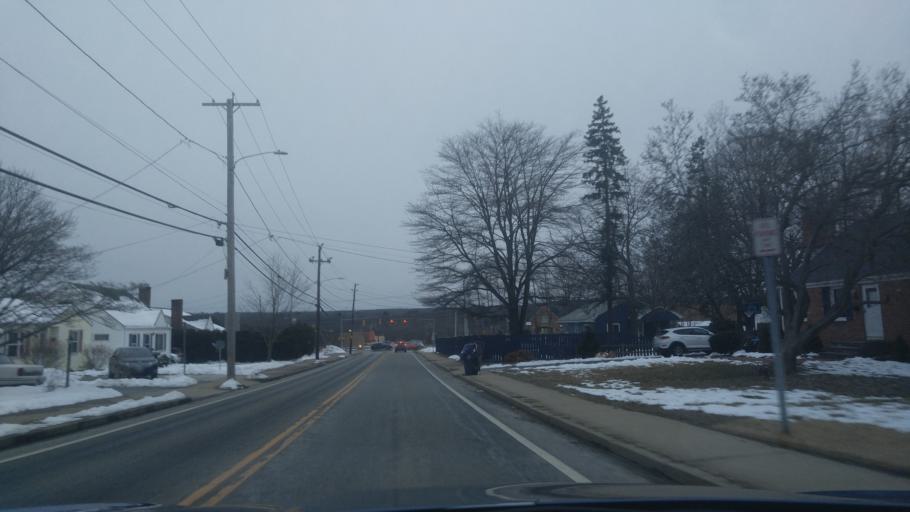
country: US
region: Rhode Island
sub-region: Kent County
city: West Warwick
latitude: 41.7342
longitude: -71.4756
